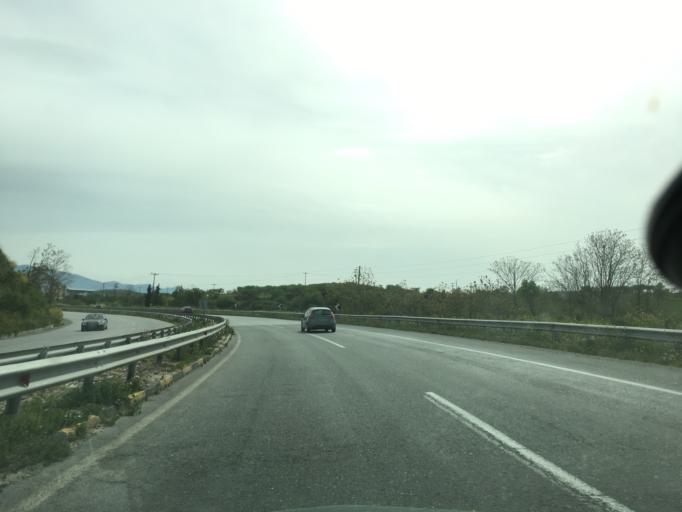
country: GR
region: Thessaly
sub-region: Nomos Magnisias
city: Velestino
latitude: 39.3811
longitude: 22.8278
